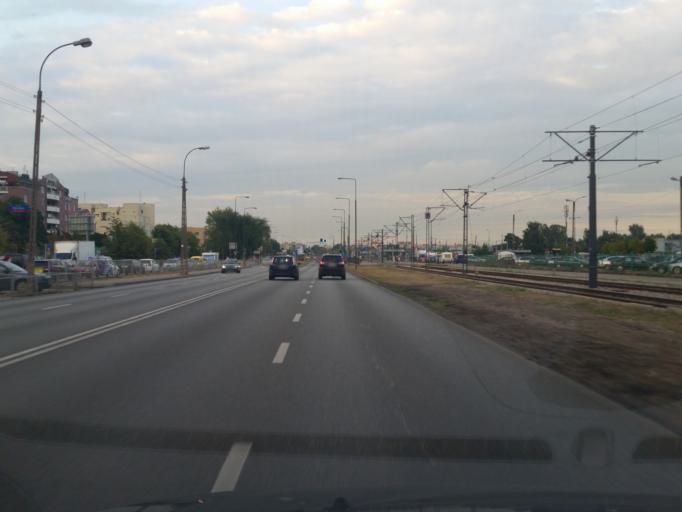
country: PL
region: Masovian Voivodeship
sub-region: Warszawa
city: Bemowo
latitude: 52.2585
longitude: 20.9213
